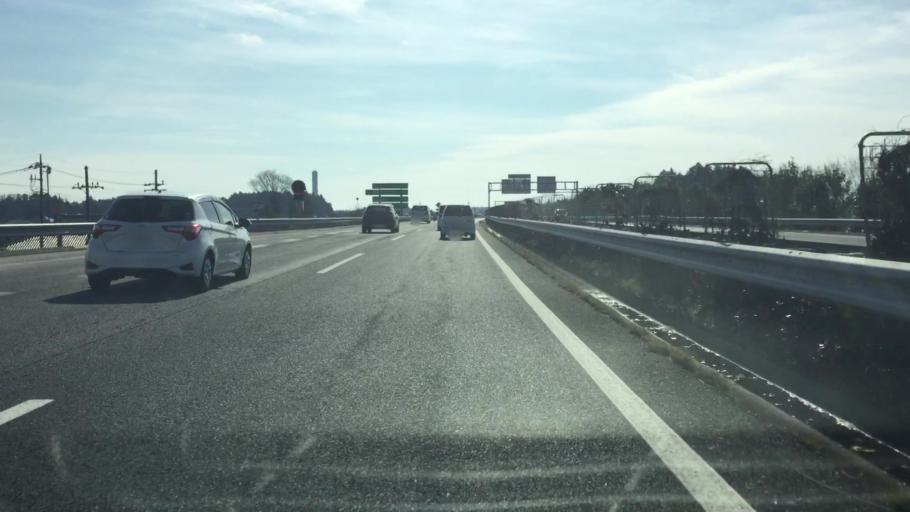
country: JP
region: Ibaraki
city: Tomobe
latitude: 36.3163
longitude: 140.3556
